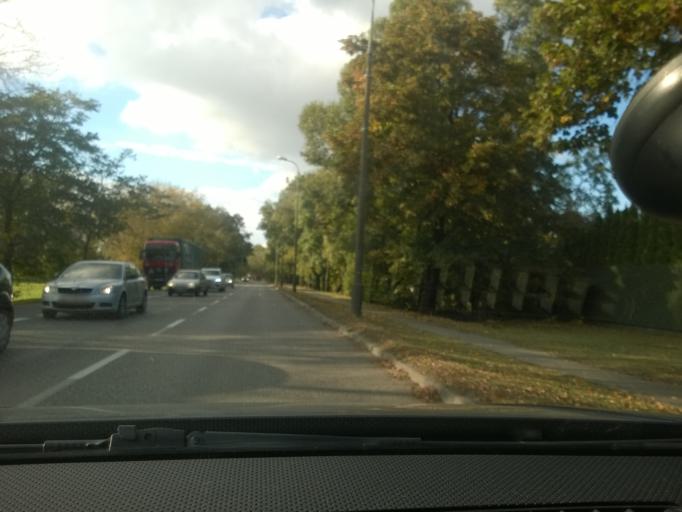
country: PL
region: Masovian Voivodeship
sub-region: Powiat pruszkowski
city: Pruszkow
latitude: 52.1737
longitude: 20.8011
